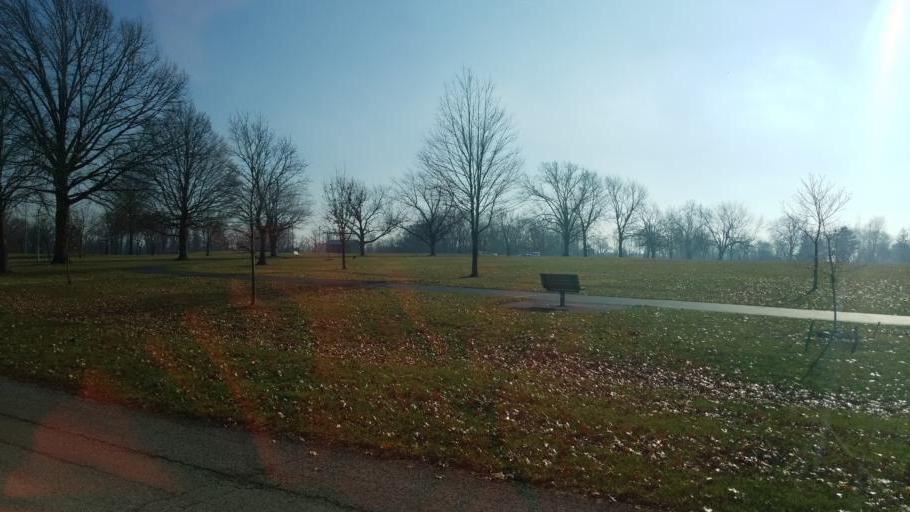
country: US
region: Ohio
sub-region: Seneca County
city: Tiffin
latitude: 41.1058
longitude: -83.1589
